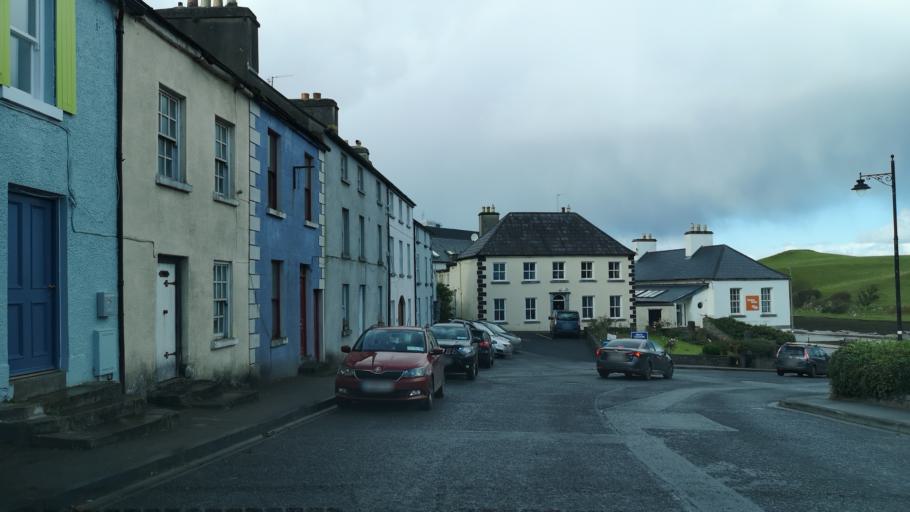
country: IE
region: Connaught
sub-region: Maigh Eo
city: Westport
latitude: 53.7997
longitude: -9.5465
